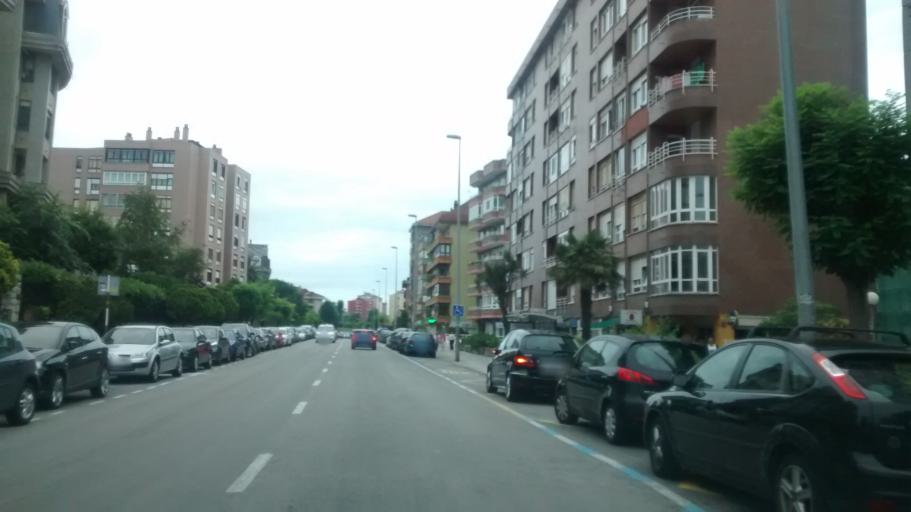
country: ES
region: Cantabria
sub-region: Provincia de Cantabria
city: Santander
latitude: 43.4686
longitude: -3.7923
